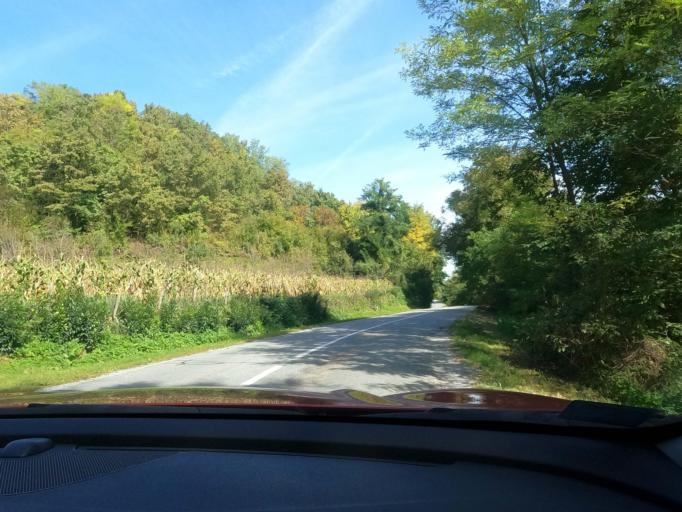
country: HR
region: Sisacko-Moslavacka
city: Petrinja
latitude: 45.3866
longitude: 16.2981
